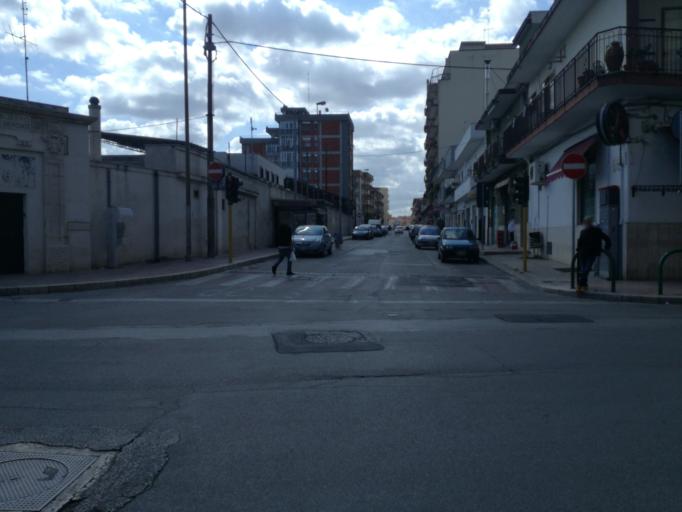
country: IT
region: Apulia
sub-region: Provincia di Bari
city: Triggiano
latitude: 41.0633
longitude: 16.9282
